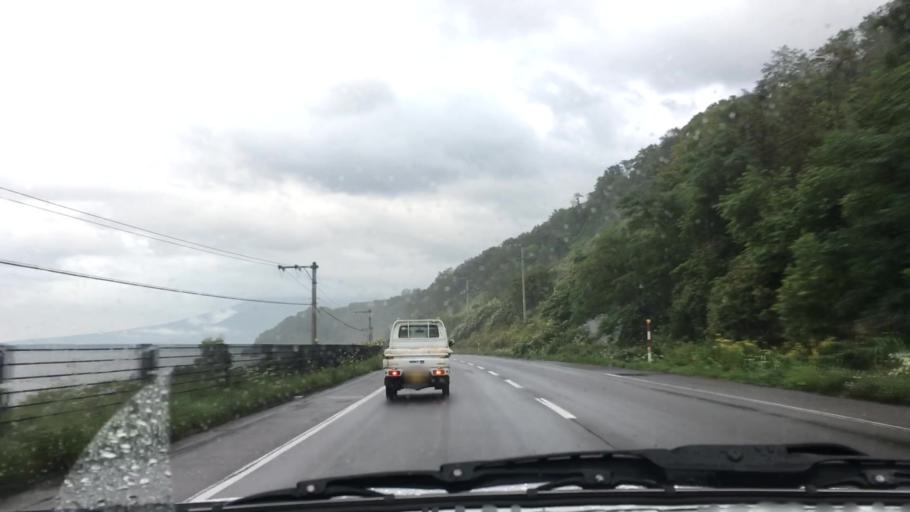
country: JP
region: Hokkaido
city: Nanae
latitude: 42.1255
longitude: 140.5200
